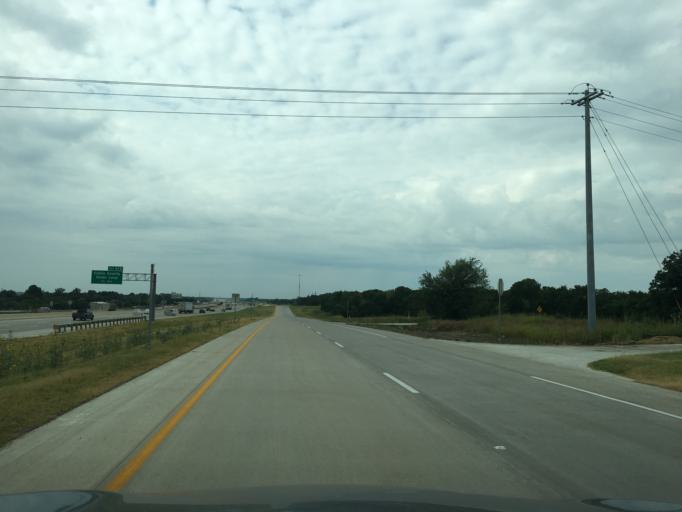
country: US
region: Texas
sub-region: Collin County
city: Anna
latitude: 33.3341
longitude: -96.5891
